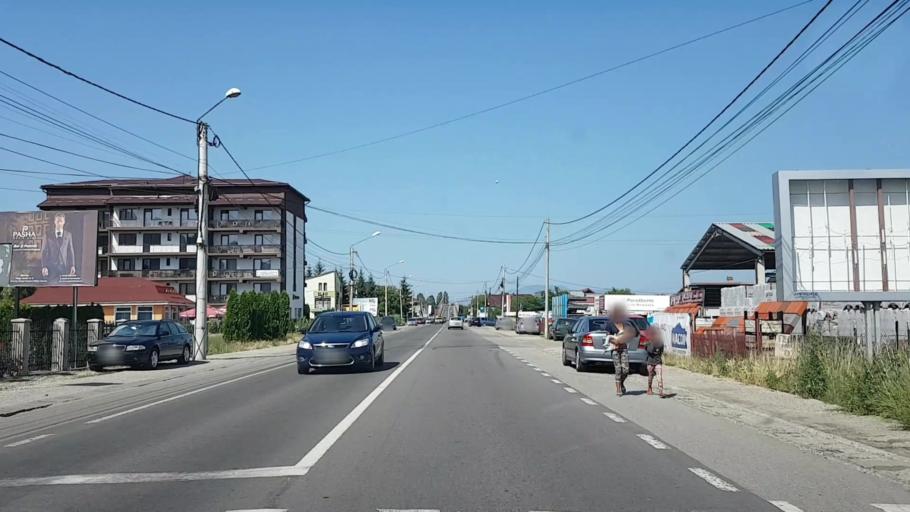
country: RO
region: Bistrita-Nasaud
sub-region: Municipiul Bistrita
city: Viisoara
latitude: 47.1124
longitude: 24.4607
